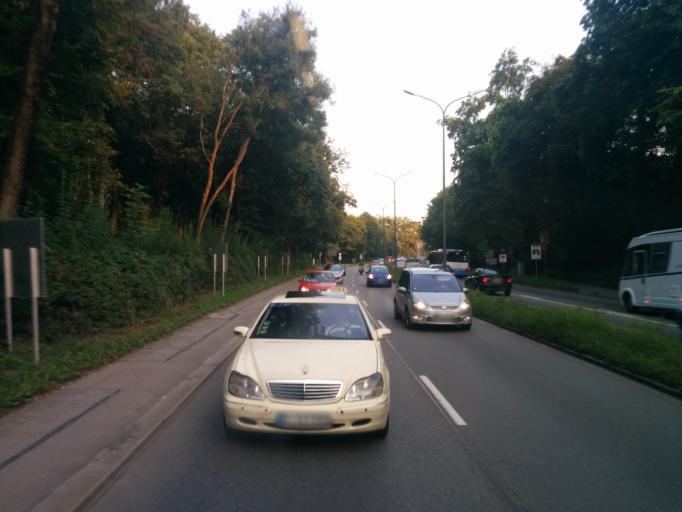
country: DE
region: Bavaria
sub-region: Upper Bavaria
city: Bogenhausen
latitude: 48.1615
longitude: 11.5995
